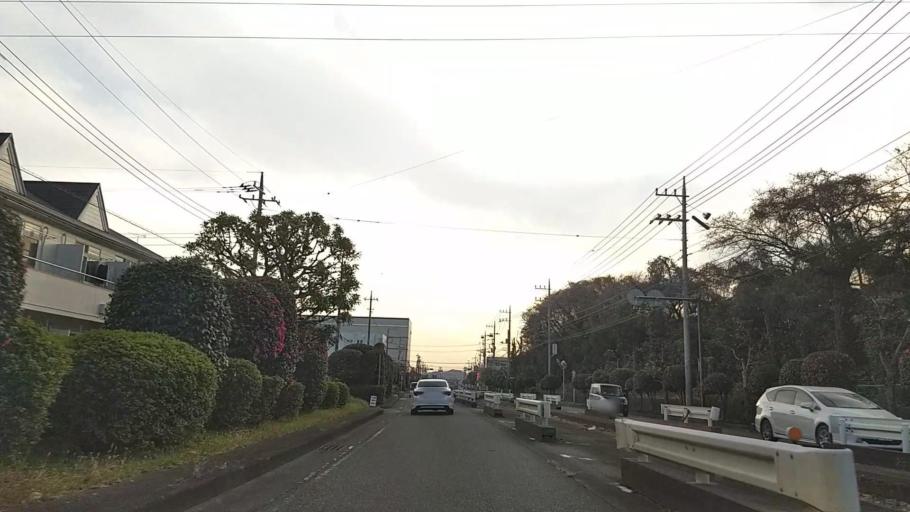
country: JP
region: Kanagawa
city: Atsugi
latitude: 35.4572
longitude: 139.3309
